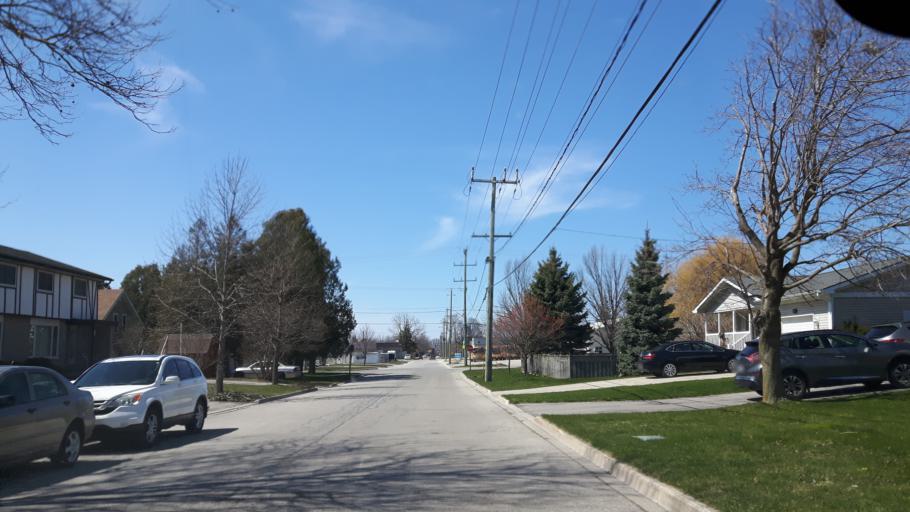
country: CA
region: Ontario
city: Goderich
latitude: 43.7363
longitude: -81.6966
